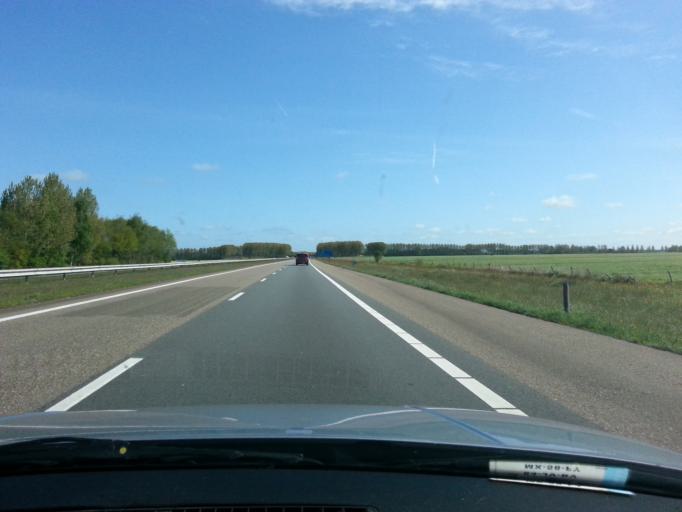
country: NL
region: Friesland
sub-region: Gemeente Opsterland
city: Tijnje
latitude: 53.0112
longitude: 6.0013
